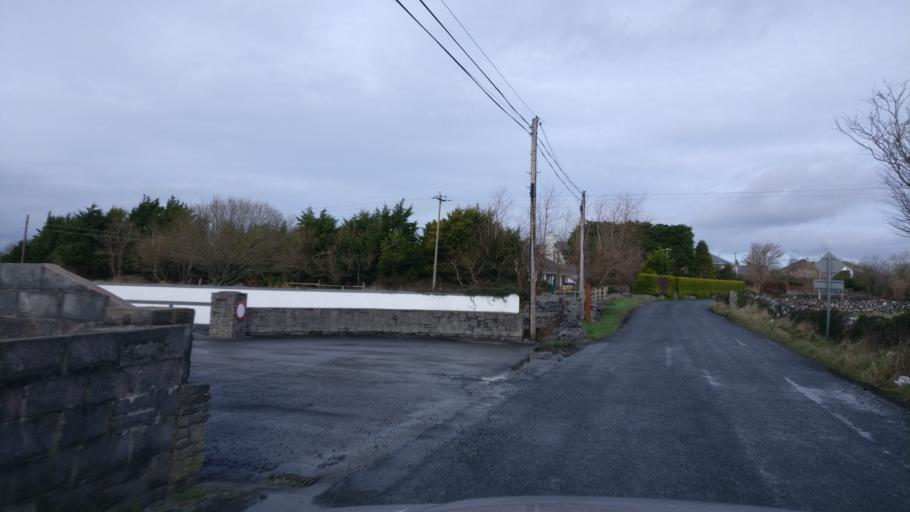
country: IE
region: Connaught
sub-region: County Galway
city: Oranmore
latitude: 53.2493
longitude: -8.9074
